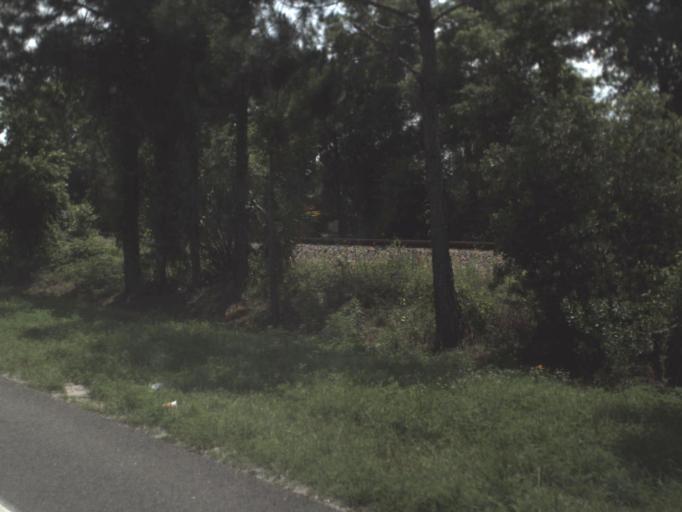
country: US
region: Florida
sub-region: Duval County
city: Jacksonville
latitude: 30.4702
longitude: -81.6317
